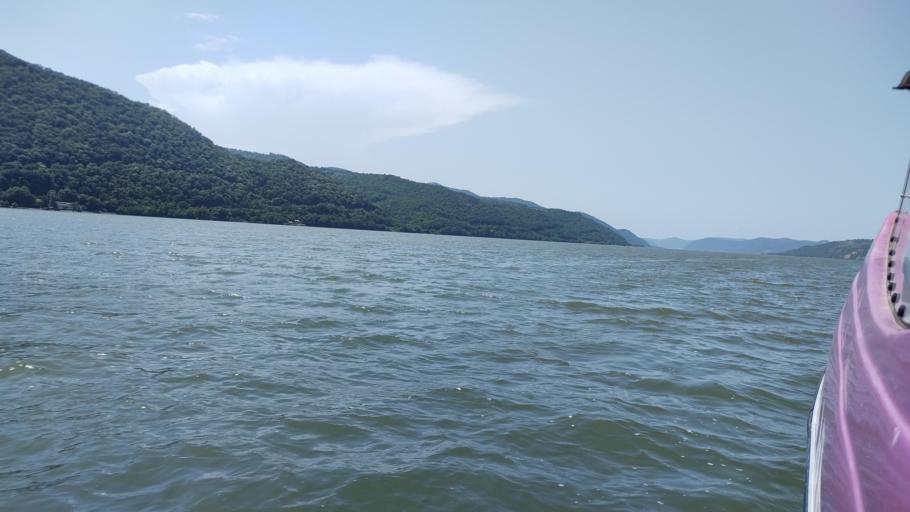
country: RO
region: Caras-Severin
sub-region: Comuna Berzasca
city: Berzasca
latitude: 44.6371
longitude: 21.9576
